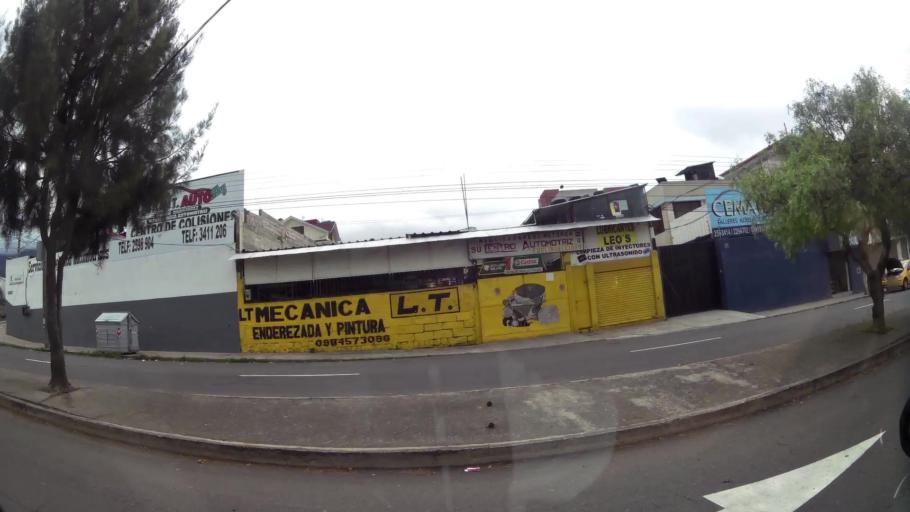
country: EC
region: Pichincha
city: Quito
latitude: -0.1222
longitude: -78.5021
